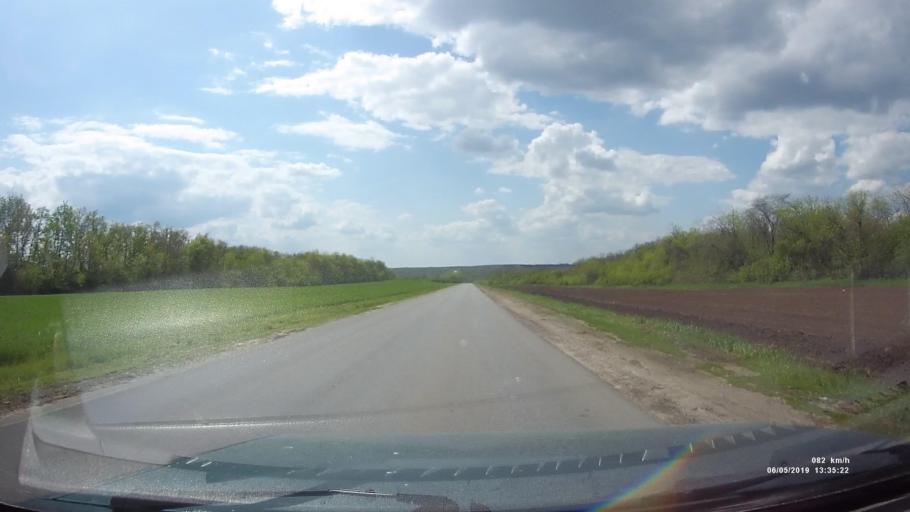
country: RU
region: Rostov
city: Ust'-Donetskiy
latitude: 47.6928
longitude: 40.7456
